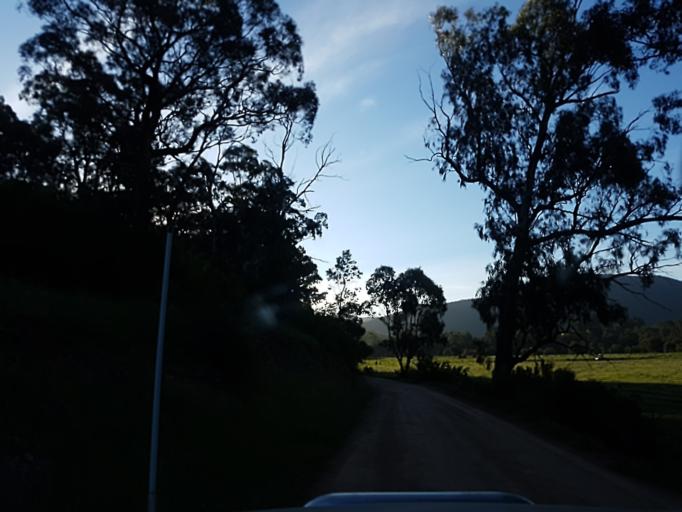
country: AU
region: Victoria
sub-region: East Gippsland
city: Bairnsdale
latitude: -37.4077
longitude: 147.1172
